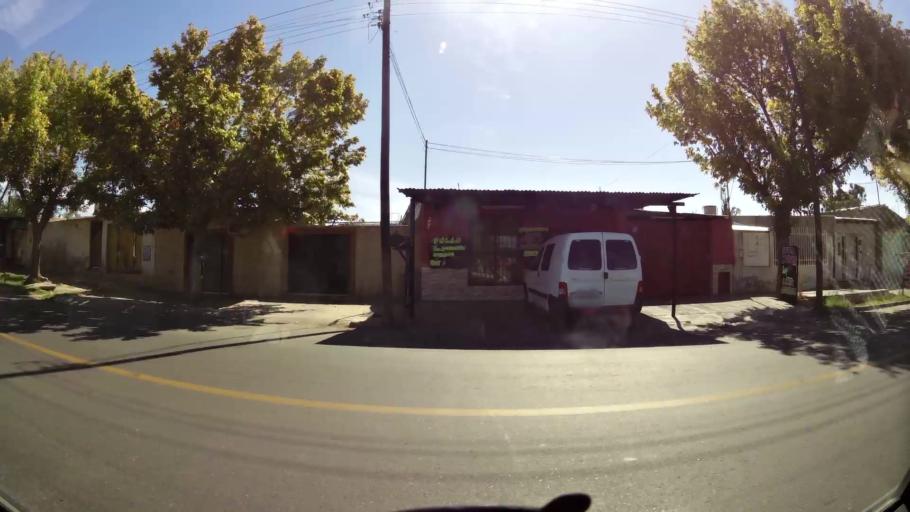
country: AR
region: Mendoza
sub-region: Departamento de Godoy Cruz
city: Godoy Cruz
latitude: -32.9546
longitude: -68.8275
